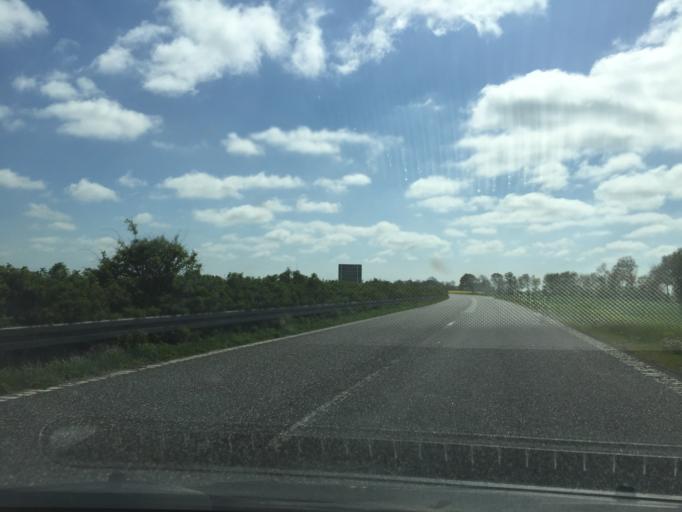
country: DK
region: Zealand
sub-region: Lolland Kommune
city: Maribo
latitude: 54.7729
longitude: 11.4661
